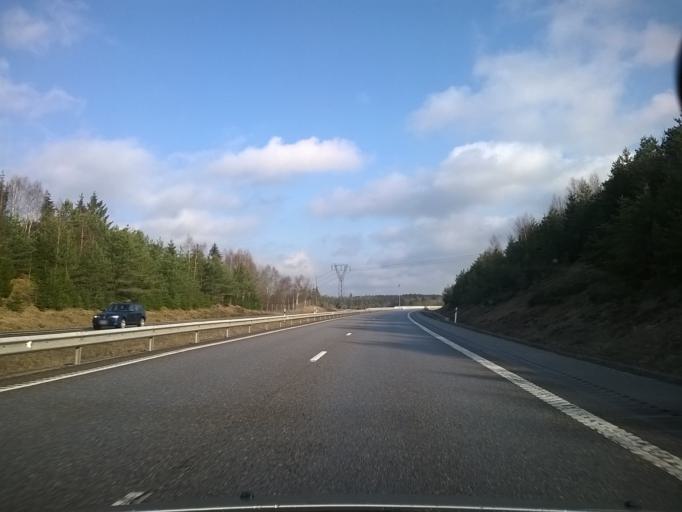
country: SE
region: Vaestra Goetaland
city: Svanesund
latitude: 58.1067
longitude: 11.8795
